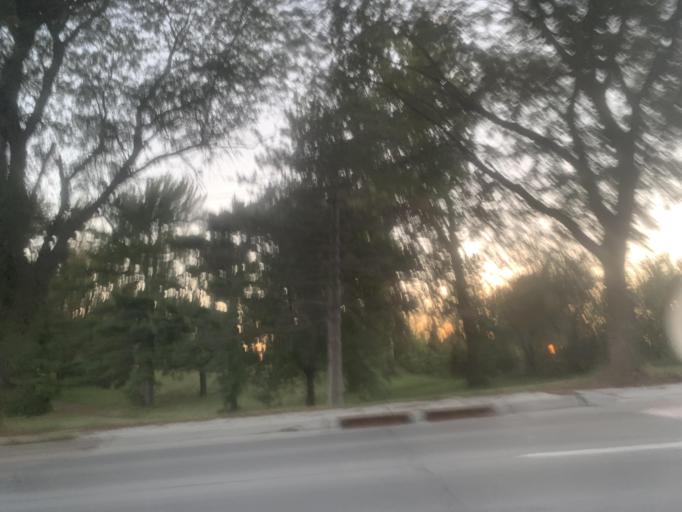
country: US
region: Nebraska
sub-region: Sarpy County
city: La Vista
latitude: 41.2097
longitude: -95.9766
